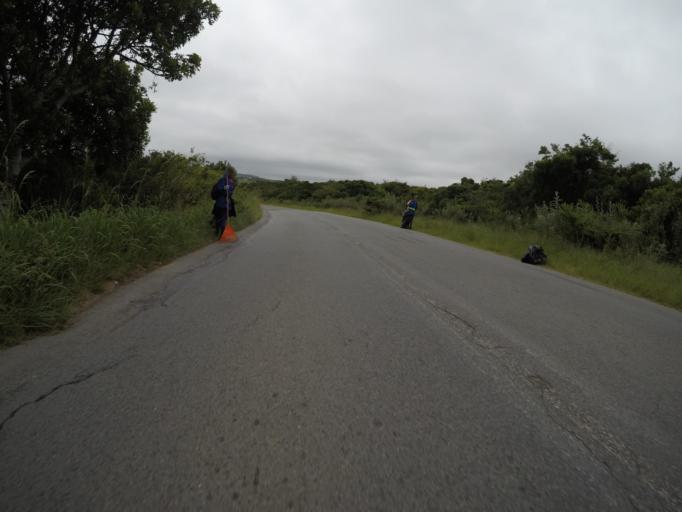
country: ZA
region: Eastern Cape
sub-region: Buffalo City Metropolitan Municipality
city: East London
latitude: -32.9455
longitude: 27.9289
